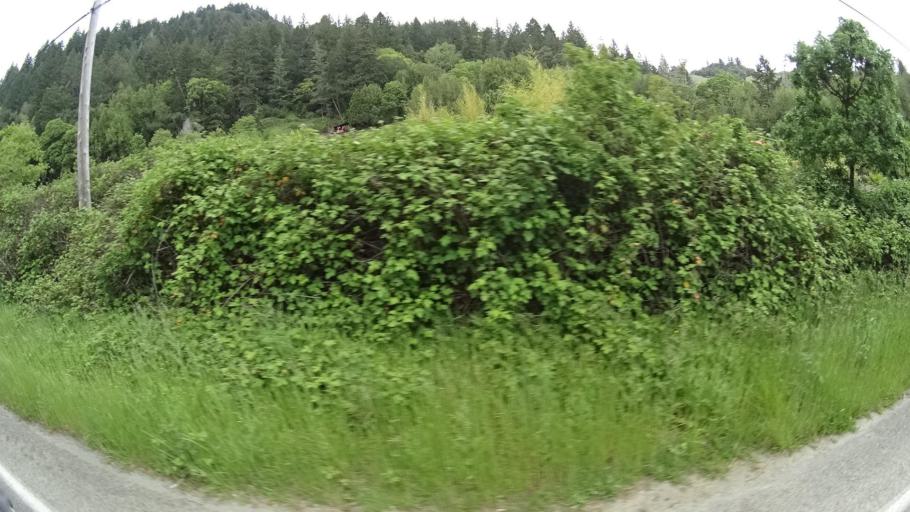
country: US
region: California
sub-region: Humboldt County
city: Redway
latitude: 40.1217
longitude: -123.8822
